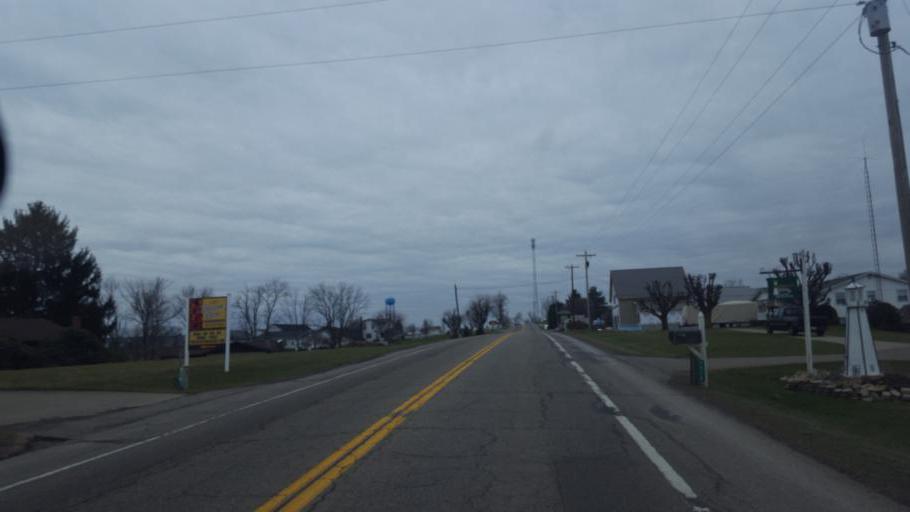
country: US
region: Ohio
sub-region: Tuscarawas County
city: Sugarcreek
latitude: 40.6033
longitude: -81.7374
